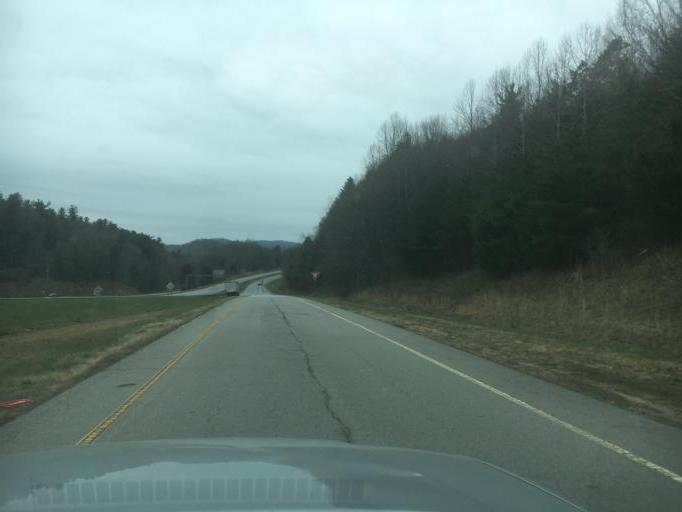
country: US
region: North Carolina
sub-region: Henderson County
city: Flat Rock
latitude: 35.2365
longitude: -82.4169
